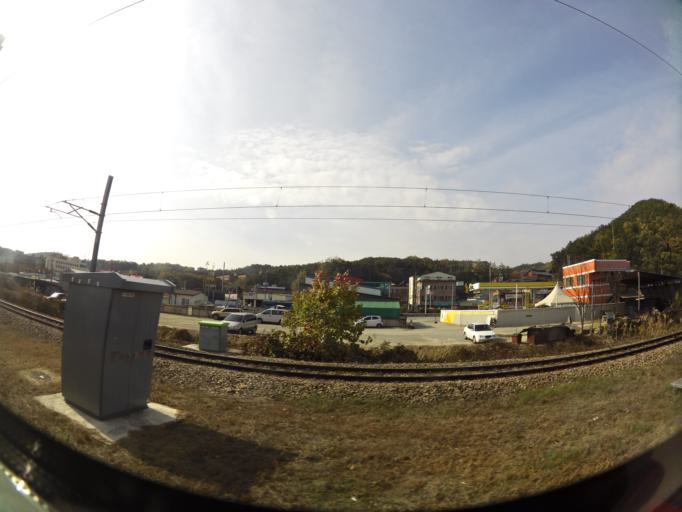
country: KR
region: Chungcheongbuk-do
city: Cheongju-si
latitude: 36.6226
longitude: 127.2915
